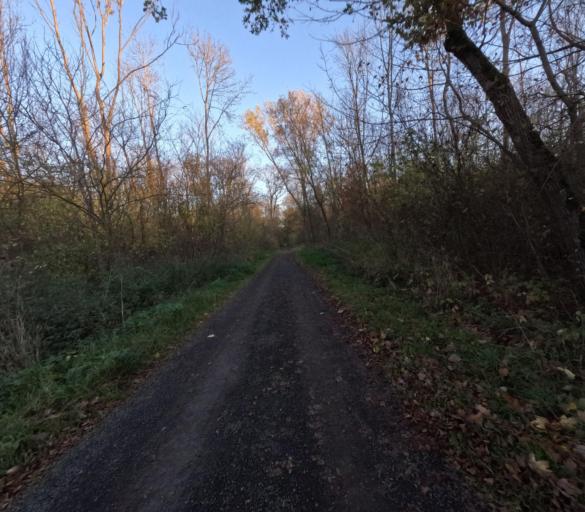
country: DE
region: Saxony
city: Schkeuditz
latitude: 51.3781
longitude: 12.2323
